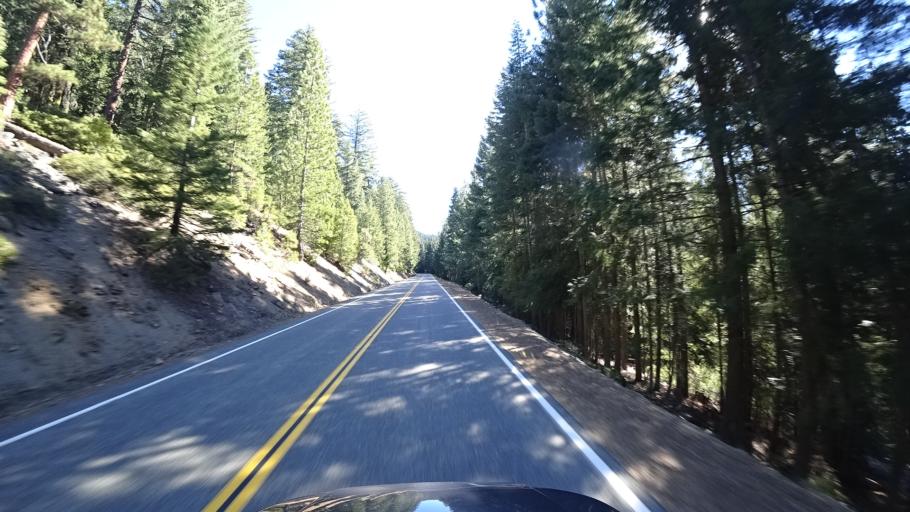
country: US
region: California
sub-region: Trinity County
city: Weaverville
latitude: 41.2291
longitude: -122.9378
